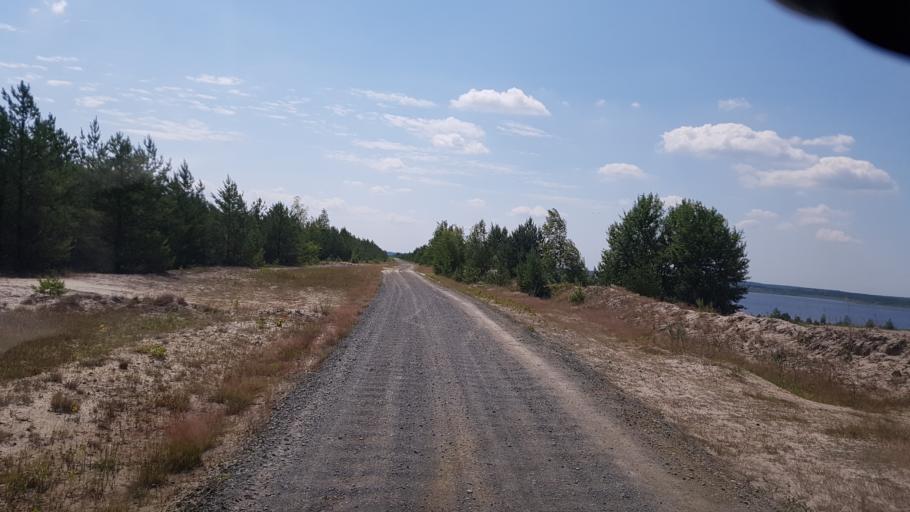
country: DE
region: Brandenburg
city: Sallgast
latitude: 51.5871
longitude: 13.7975
